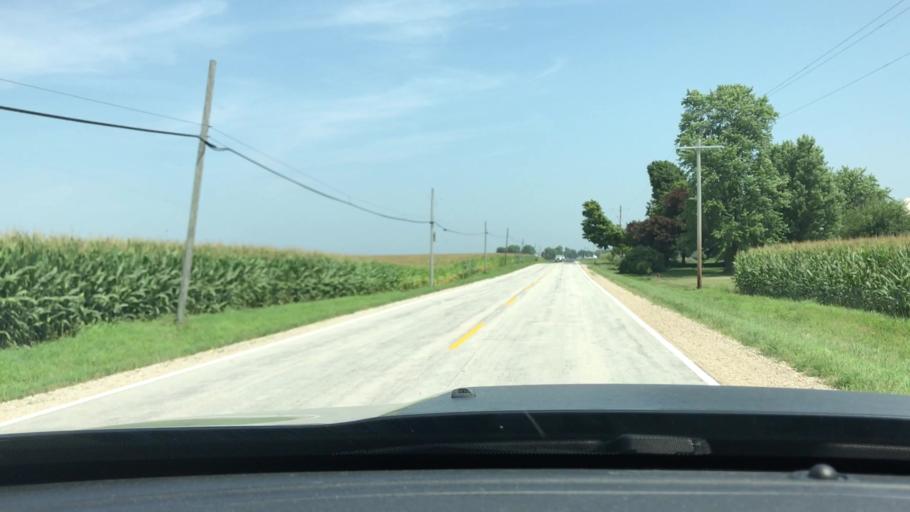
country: US
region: Illinois
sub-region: LaSalle County
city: Sheridan
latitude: 41.5033
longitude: -88.7309
